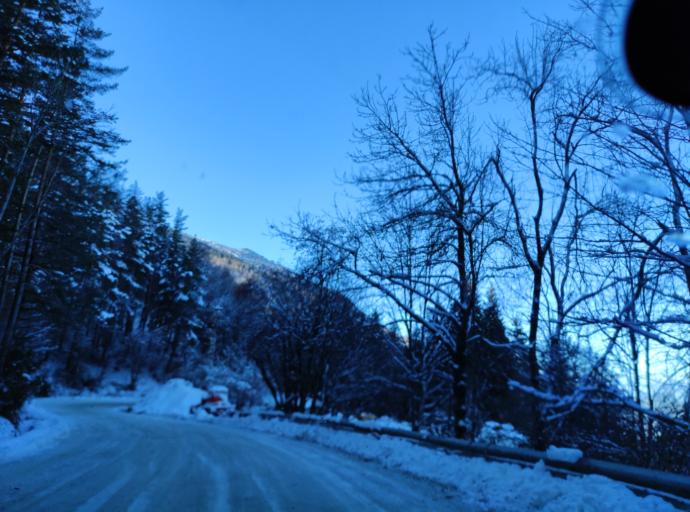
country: BG
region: Sofia-Capital
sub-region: Stolichna Obshtina
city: Sofia
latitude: 42.6044
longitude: 23.3008
